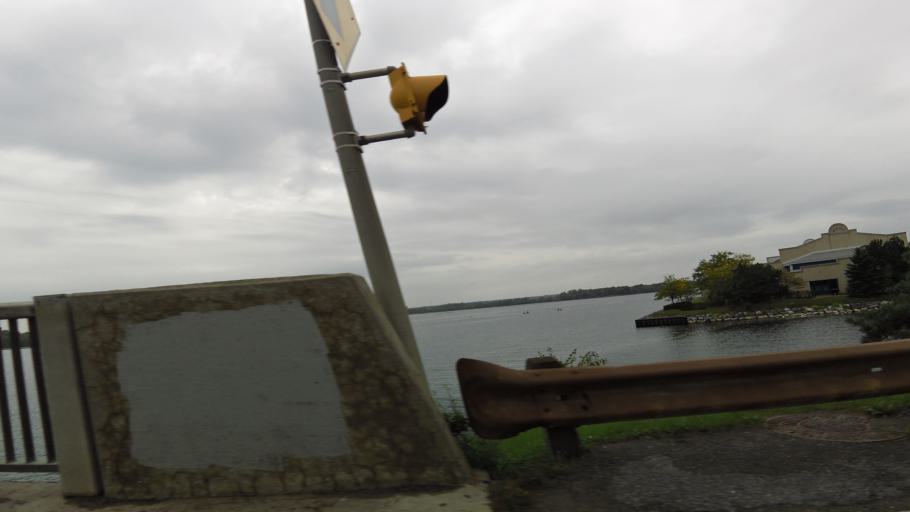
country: CA
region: Ontario
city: Kingston
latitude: 44.2351
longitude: -76.4711
